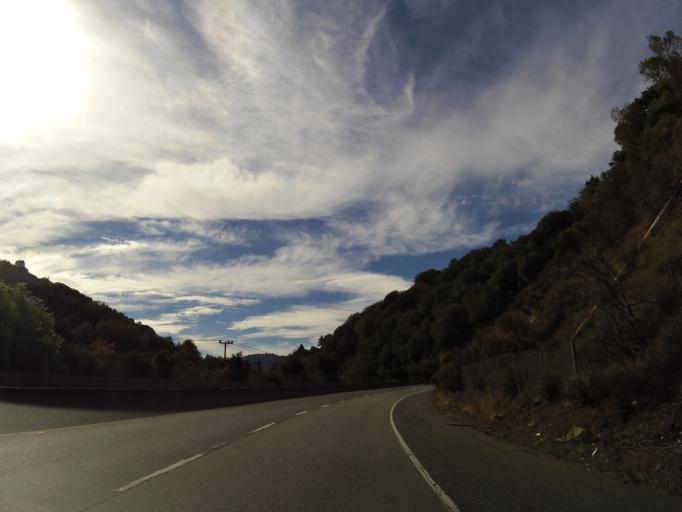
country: US
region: California
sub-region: Santa Clara County
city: Los Gatos
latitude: 37.2129
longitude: -121.9881
